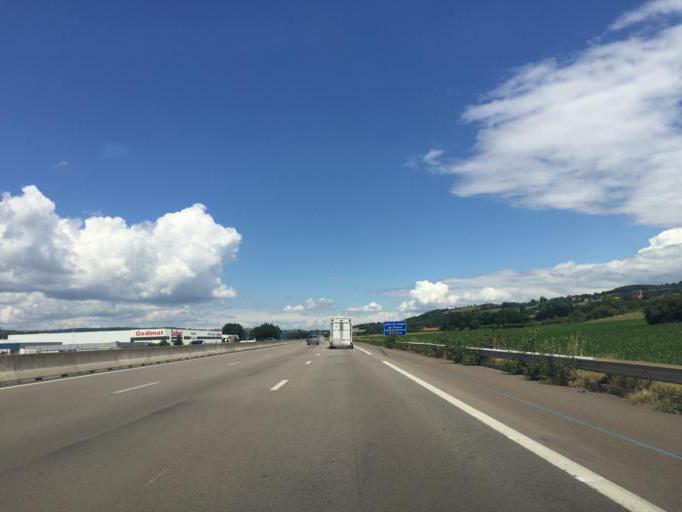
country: FR
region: Rhone-Alpes
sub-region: Departement de l'Isere
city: Reventin-Vaugris
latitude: 45.4601
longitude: 4.8322
